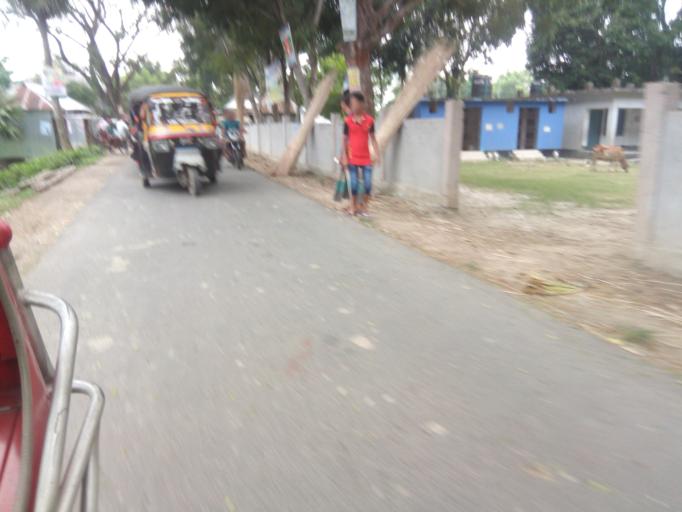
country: BD
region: Khulna
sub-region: Magura
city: Magura
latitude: 23.5069
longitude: 89.6123
